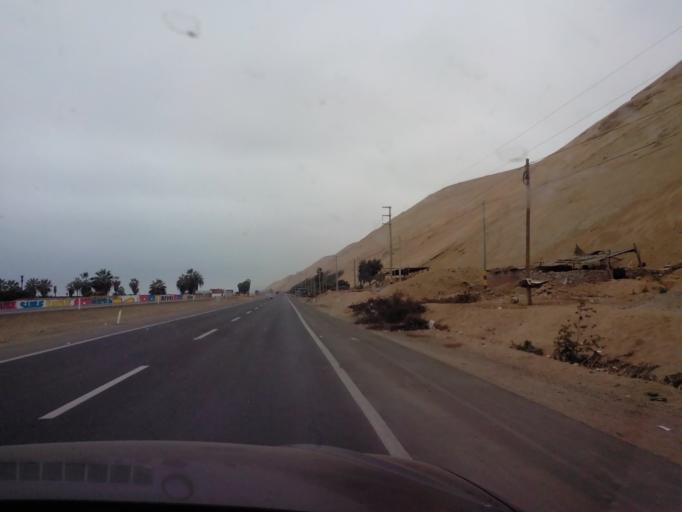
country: PE
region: Ica
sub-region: Provincia de Chincha
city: San Pedro
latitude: -13.3500
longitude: -76.2239
